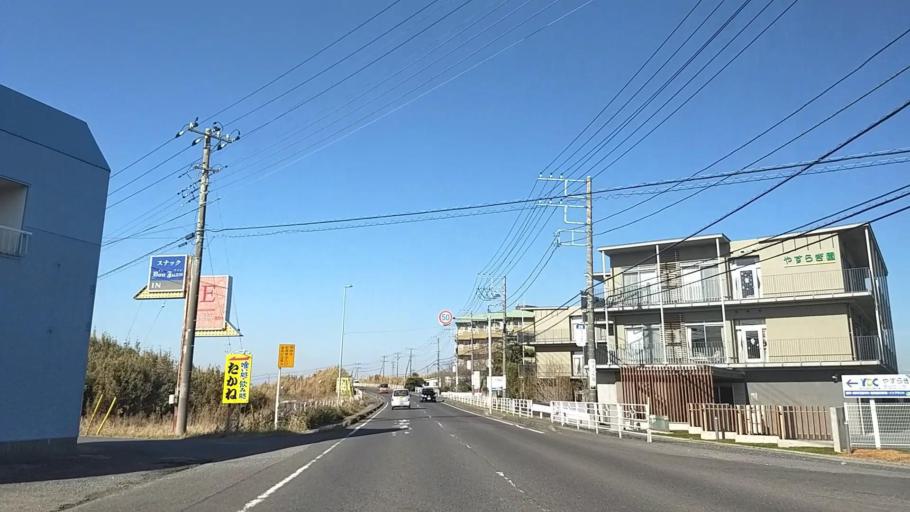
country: JP
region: Chiba
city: Asahi
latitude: 35.7247
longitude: 140.6727
